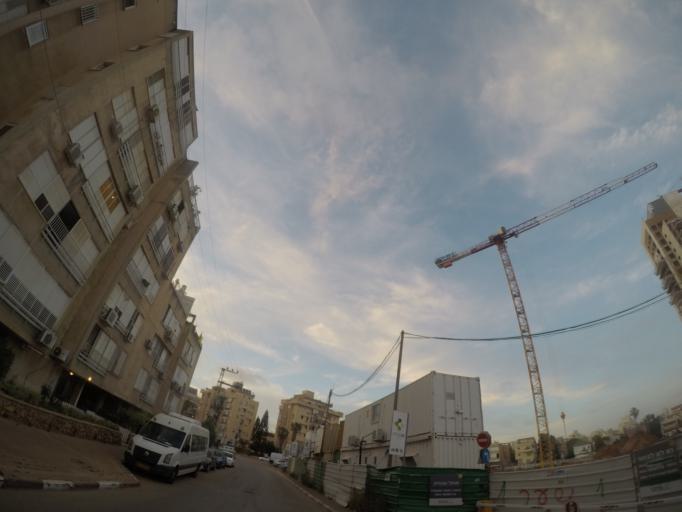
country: IL
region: Central District
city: Netanya
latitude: 32.3335
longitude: 34.8614
